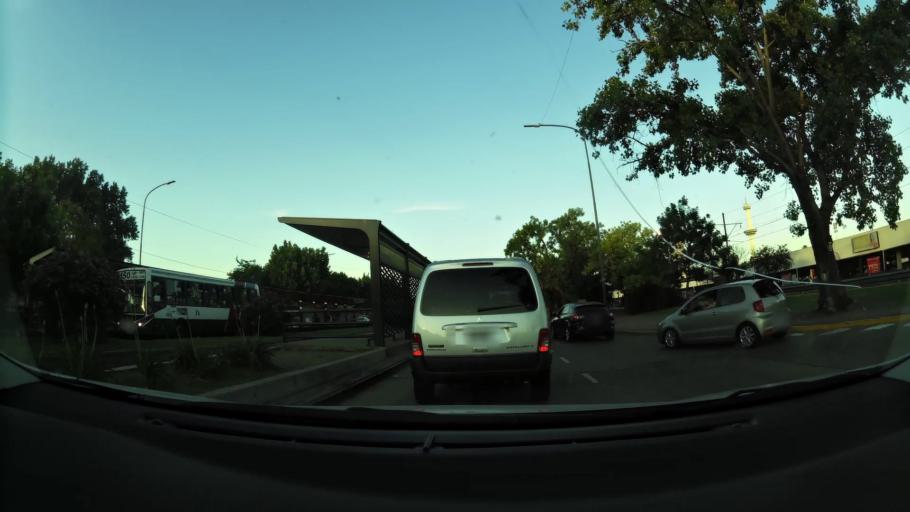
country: AR
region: Buenos Aires F.D.
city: Villa Lugano
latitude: -34.6748
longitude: -58.4607
